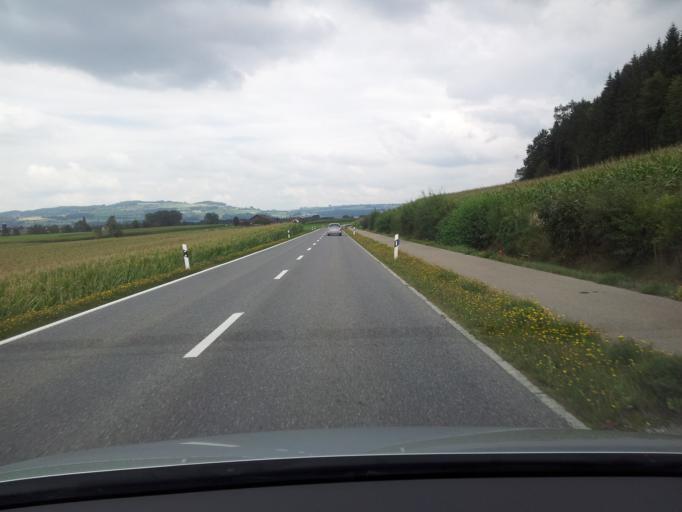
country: CH
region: Lucerne
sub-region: Sursee District
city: Mauensee
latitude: 47.1674
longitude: 8.0544
